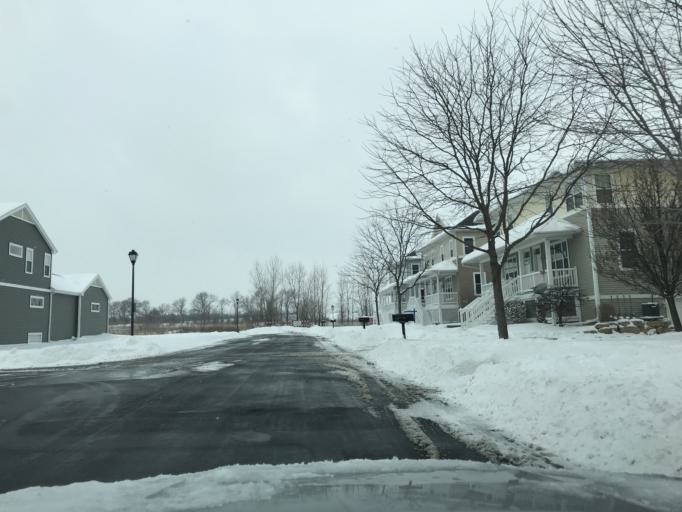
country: US
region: Wisconsin
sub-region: Dane County
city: Sun Prairie
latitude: 43.1679
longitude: -89.2783
